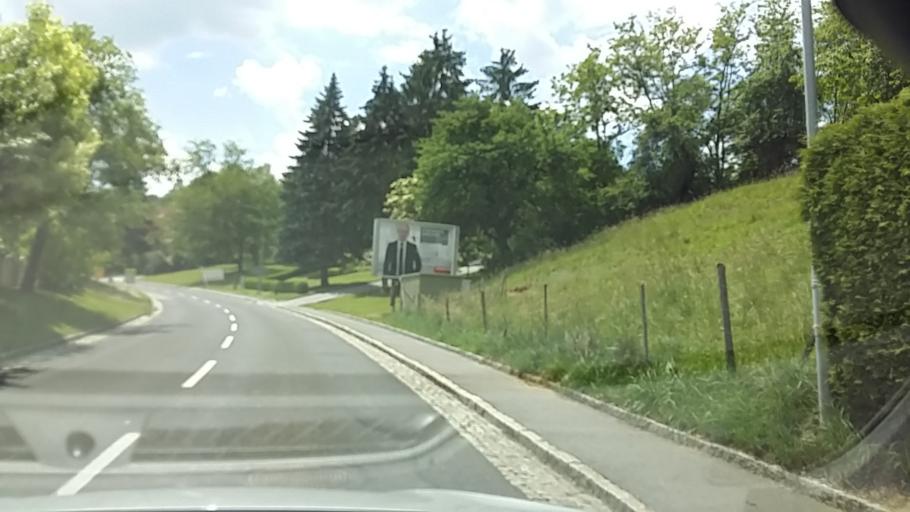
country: AT
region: Styria
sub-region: Politischer Bezirk Hartberg-Fuerstenfeld
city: Burgau
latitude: 47.1407
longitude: 16.0954
